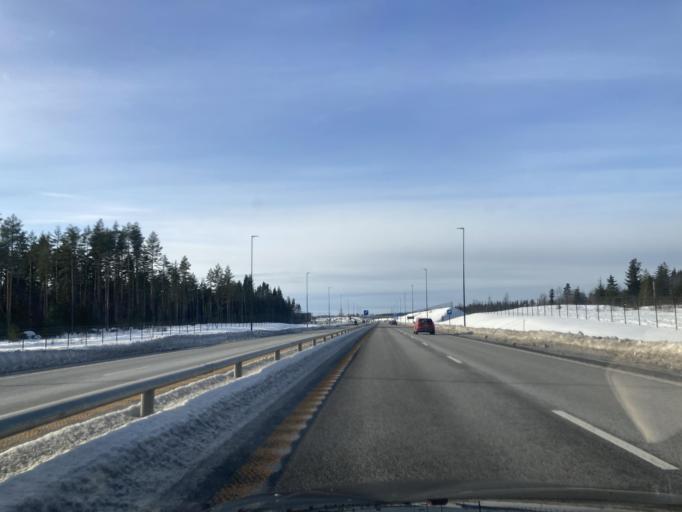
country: NO
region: Hedmark
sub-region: Loten
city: Loten
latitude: 60.8523
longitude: 11.3861
